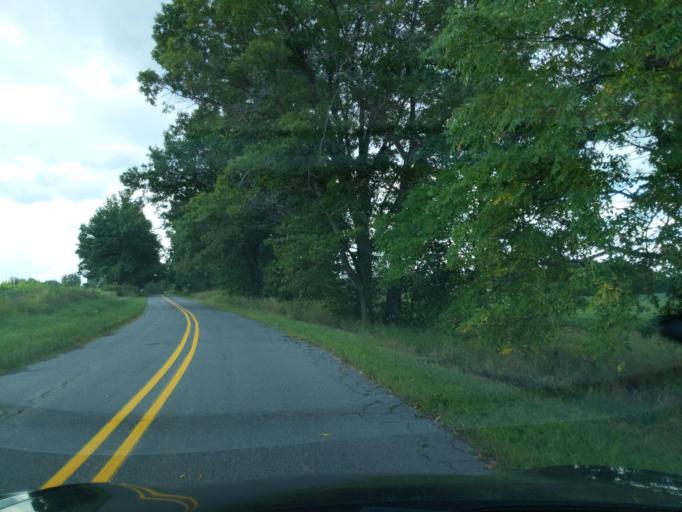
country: US
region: Michigan
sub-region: Eaton County
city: Eaton Rapids
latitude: 42.4215
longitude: -84.5807
